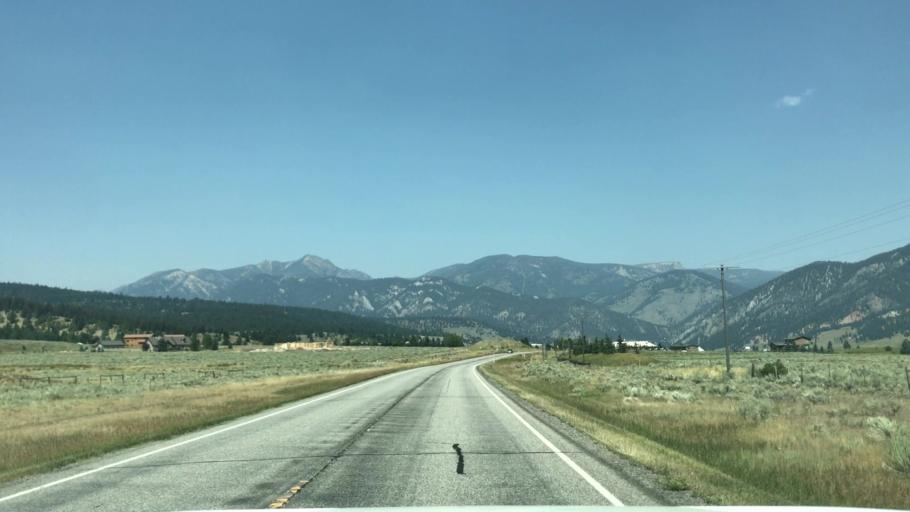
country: US
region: Montana
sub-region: Gallatin County
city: Big Sky
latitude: 45.2185
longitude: -111.2498
